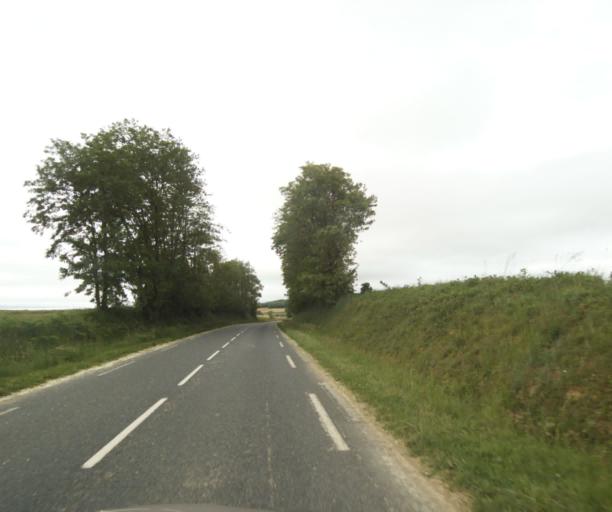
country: FR
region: Rhone-Alpes
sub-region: Departement de l'Ain
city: Miribel
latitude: 45.8360
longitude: 4.9452
